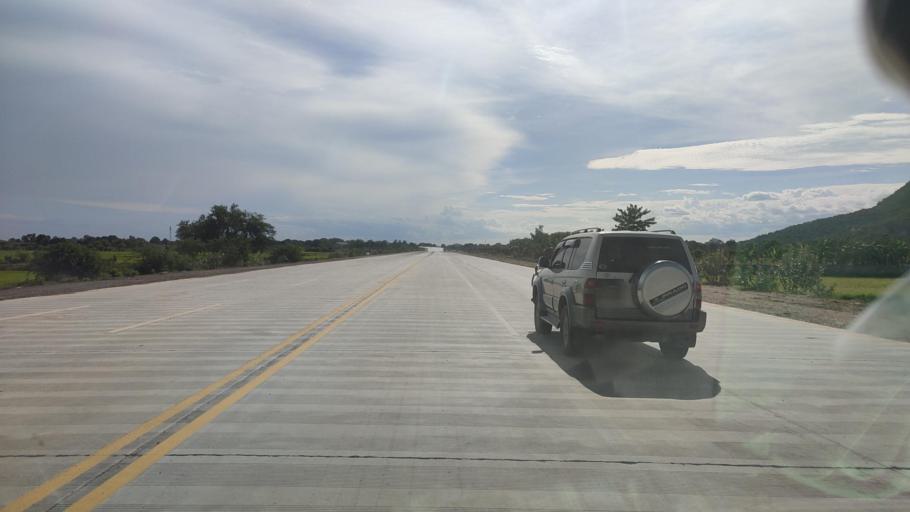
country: MM
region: Mandalay
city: Kyaukse
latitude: 21.5957
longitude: 96.1629
